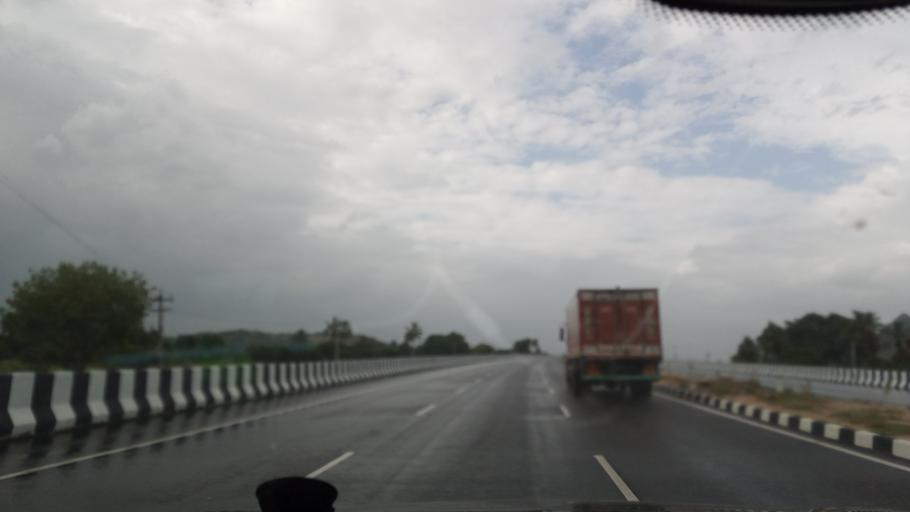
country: IN
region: Andhra Pradesh
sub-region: Chittoor
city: Chittoor
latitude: 13.2937
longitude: 79.0484
